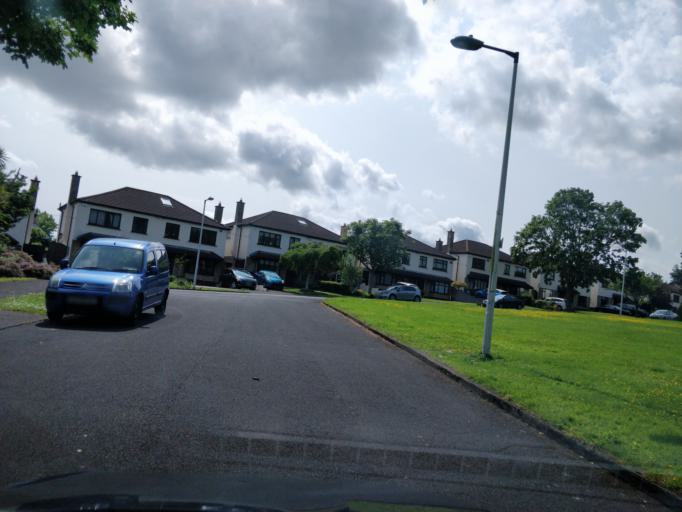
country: IE
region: Leinster
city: Balally
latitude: 53.2911
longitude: -6.2325
